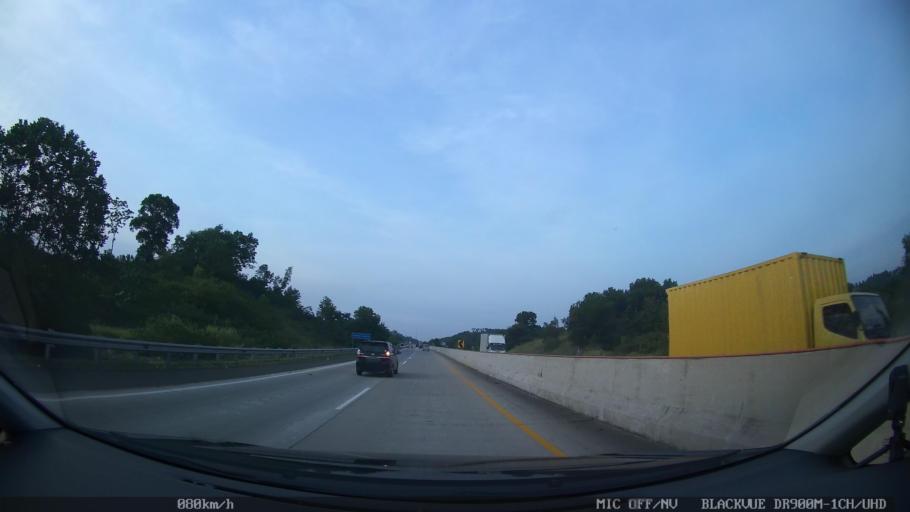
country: ID
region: Lampung
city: Penengahan
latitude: -5.8370
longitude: 105.7302
